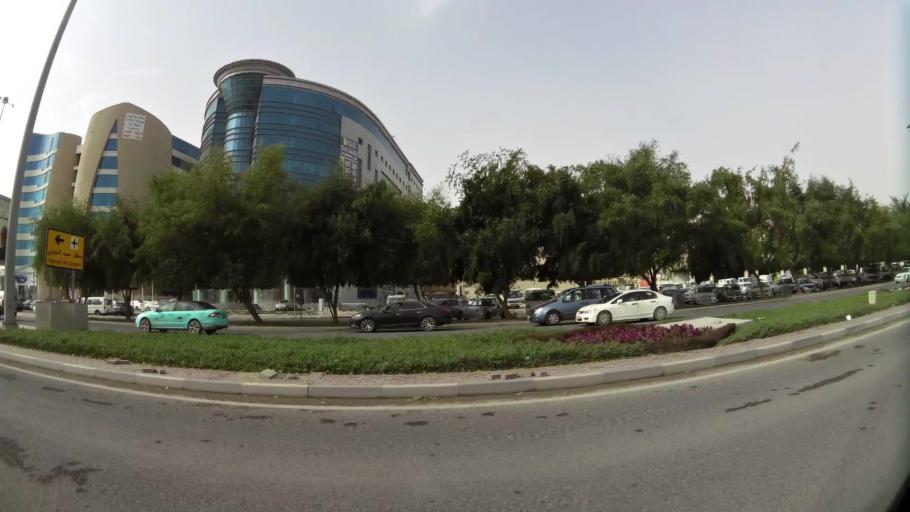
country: QA
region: Baladiyat ad Dawhah
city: Doha
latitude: 25.2706
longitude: 51.5470
